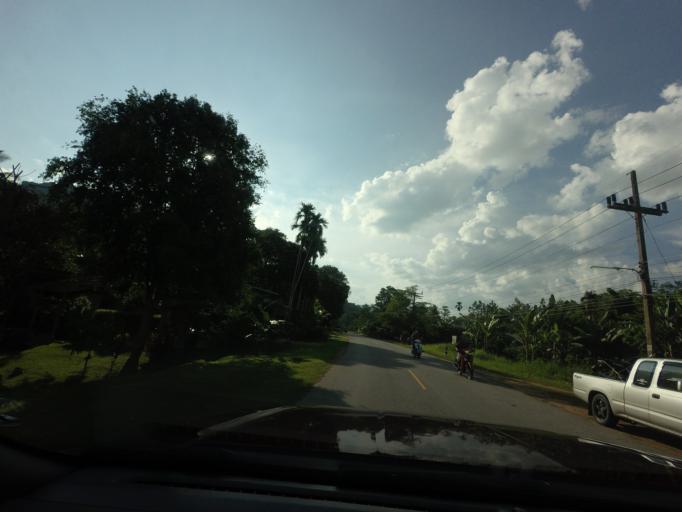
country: TH
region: Yala
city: Than To
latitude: 6.2034
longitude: 101.2371
